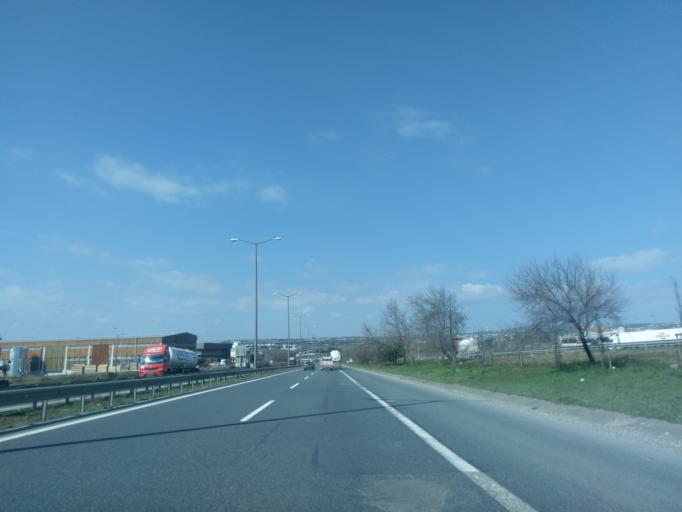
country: TR
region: Istanbul
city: Ortakoy
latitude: 41.0844
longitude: 28.3689
